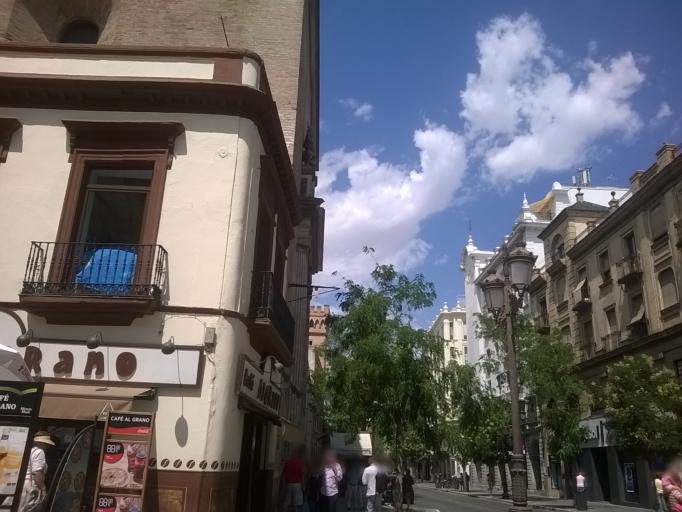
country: ES
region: Andalusia
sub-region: Provincia de Sevilla
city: Sevilla
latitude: 37.3928
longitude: -5.9922
